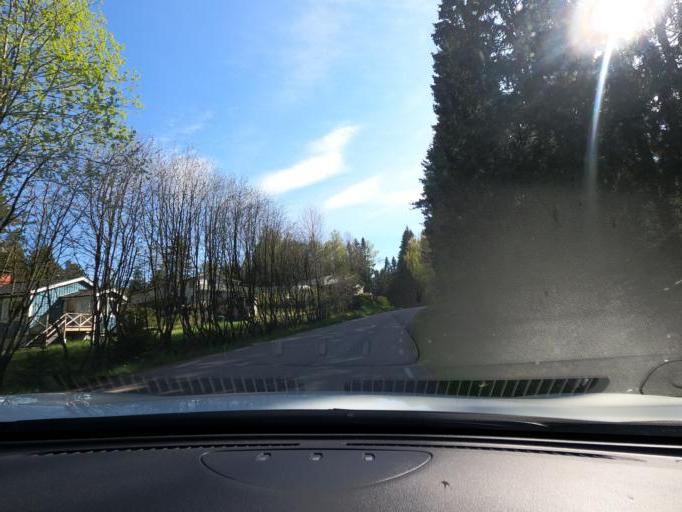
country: SE
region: Vaestra Goetaland
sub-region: Harryda Kommun
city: Hindas
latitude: 57.6499
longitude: 12.3585
